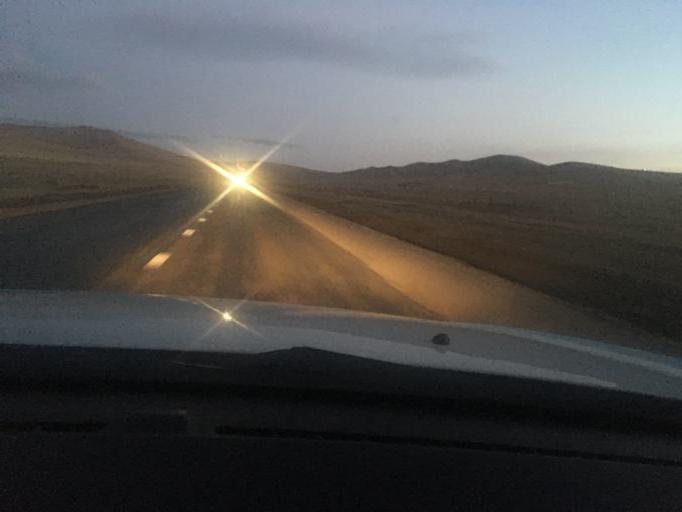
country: MN
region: Ulaanbaatar
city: Ulaanbaatar
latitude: 47.9870
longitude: 106.5630
